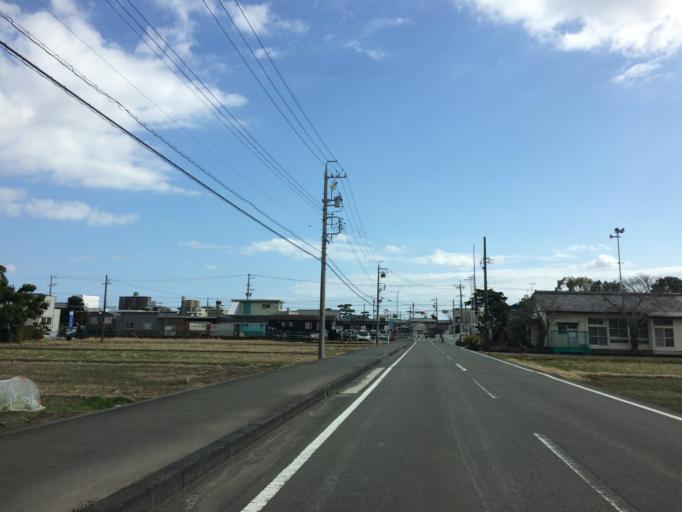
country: JP
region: Shizuoka
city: Fujieda
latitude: 34.8532
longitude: 138.2412
